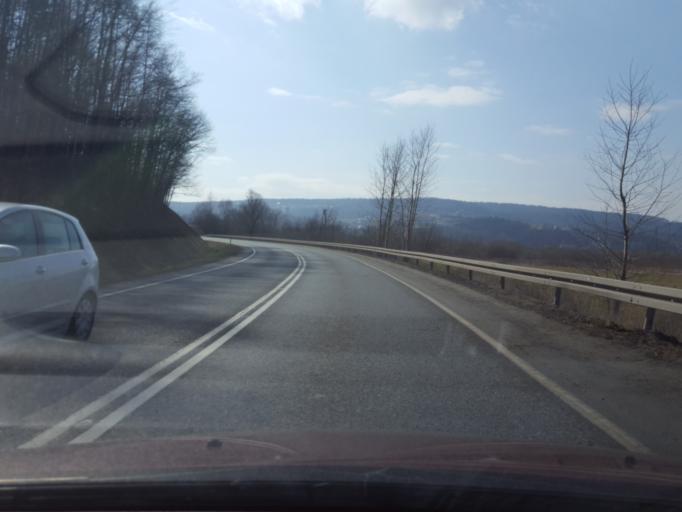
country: PL
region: Lesser Poland Voivodeship
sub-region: Powiat nowosadecki
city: Chelmiec
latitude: 49.6805
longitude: 20.6530
